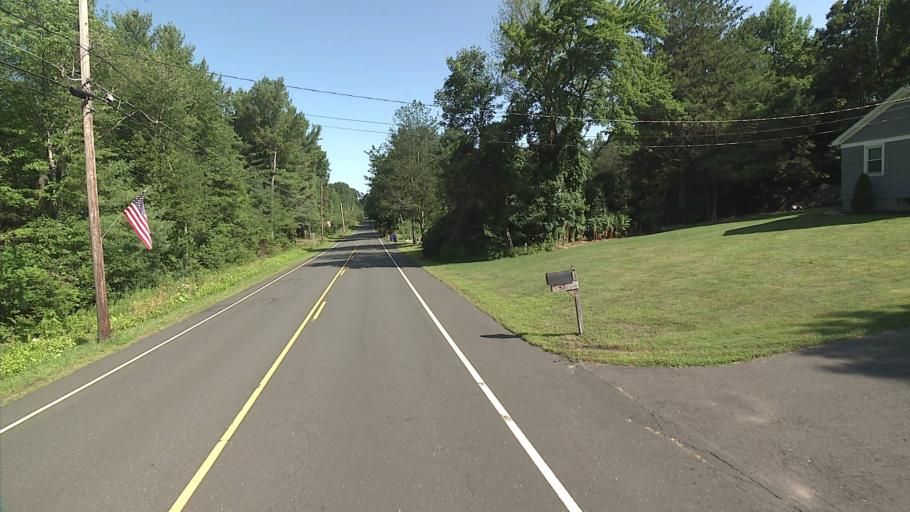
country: US
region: Connecticut
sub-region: Hartford County
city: North Granby
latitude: 42.0013
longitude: -72.9077
